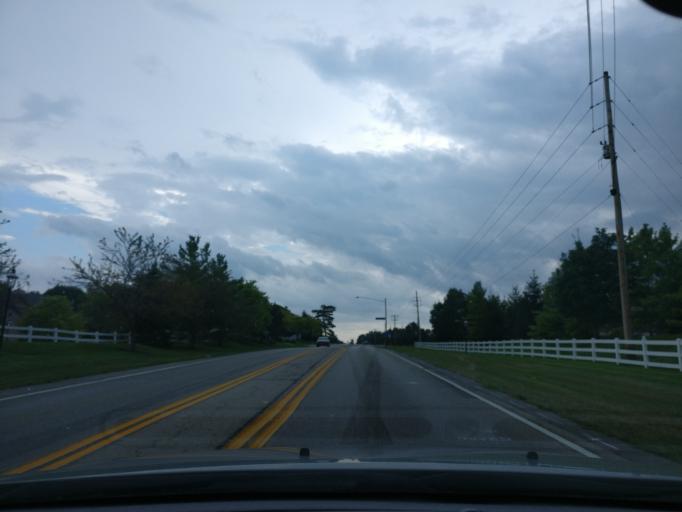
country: US
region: Ohio
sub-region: Warren County
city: Five Points
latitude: 39.6041
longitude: -84.1995
